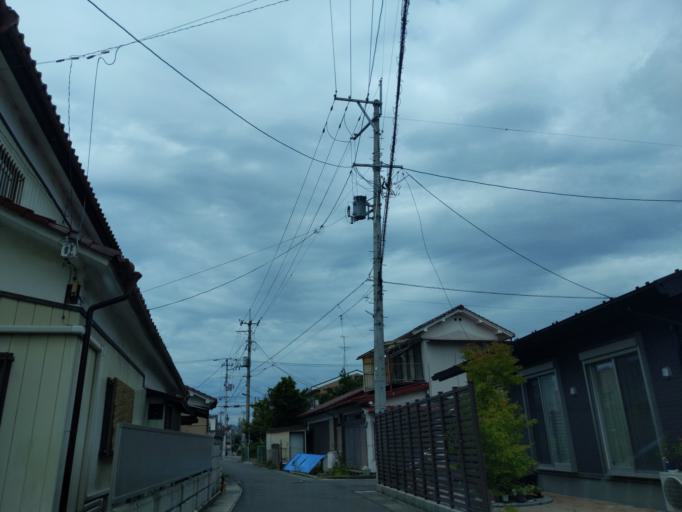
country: JP
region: Fukushima
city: Koriyama
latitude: 37.3832
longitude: 140.3828
